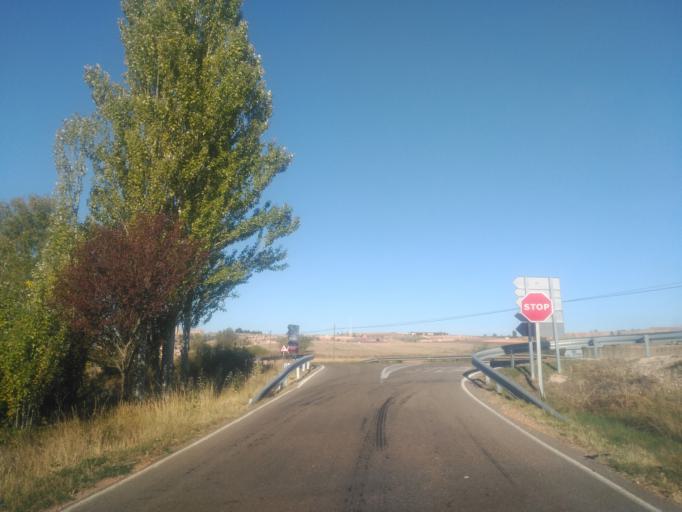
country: ES
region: Castille and Leon
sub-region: Provincia de Burgos
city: Penaranda de Duero
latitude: 41.6889
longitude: -3.4658
